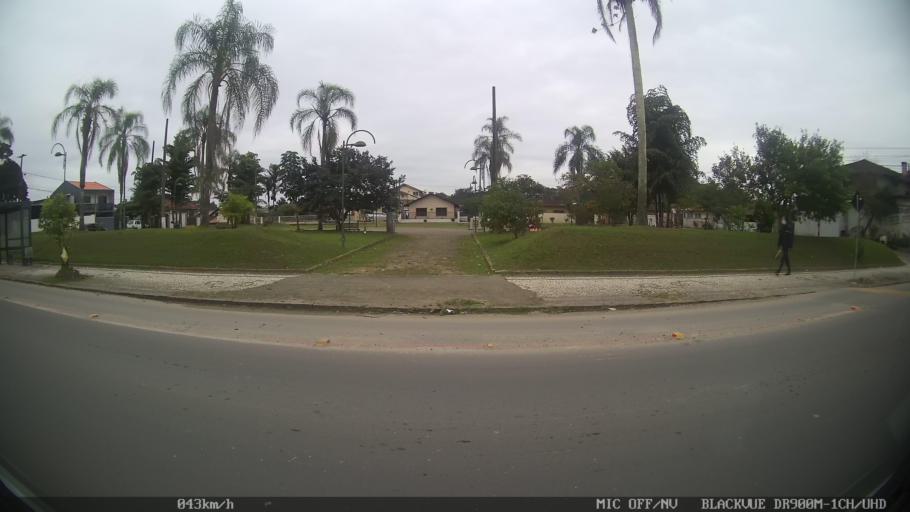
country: BR
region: Santa Catarina
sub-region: Joinville
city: Joinville
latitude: -26.3269
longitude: -48.8175
